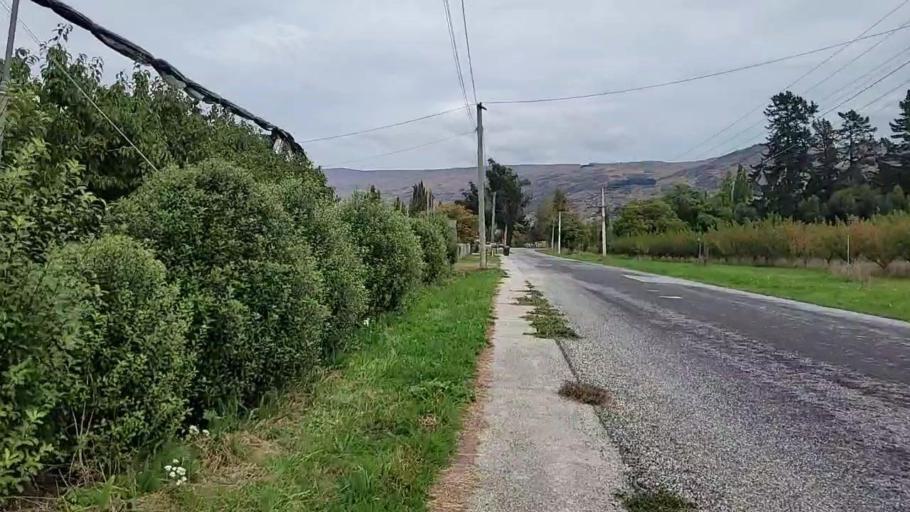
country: NZ
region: Otago
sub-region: Queenstown-Lakes District
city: Kingston
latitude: -45.4810
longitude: 169.3131
